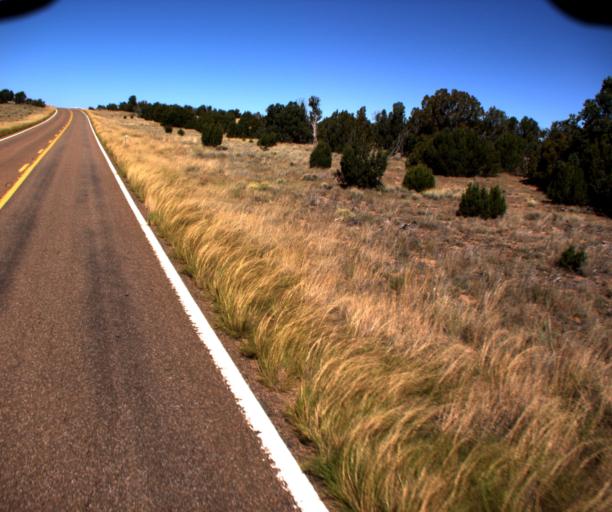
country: US
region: Arizona
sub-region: Navajo County
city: Heber-Overgaard
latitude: 34.4614
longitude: -110.4705
